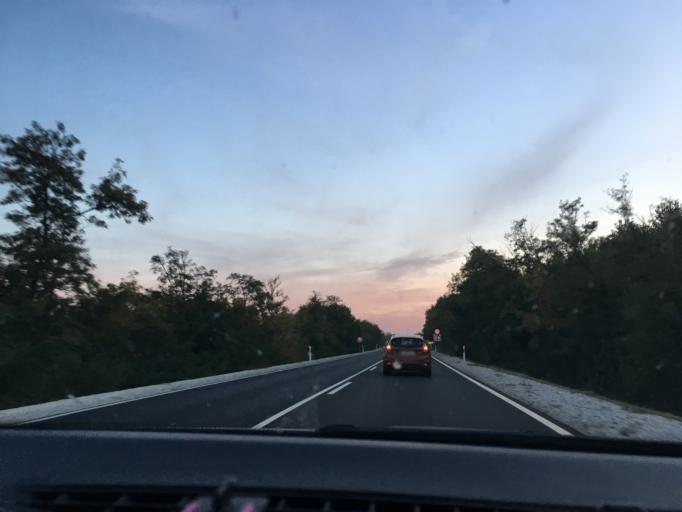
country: HU
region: Hajdu-Bihar
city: Debrecen
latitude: 47.6039
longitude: 21.6552
